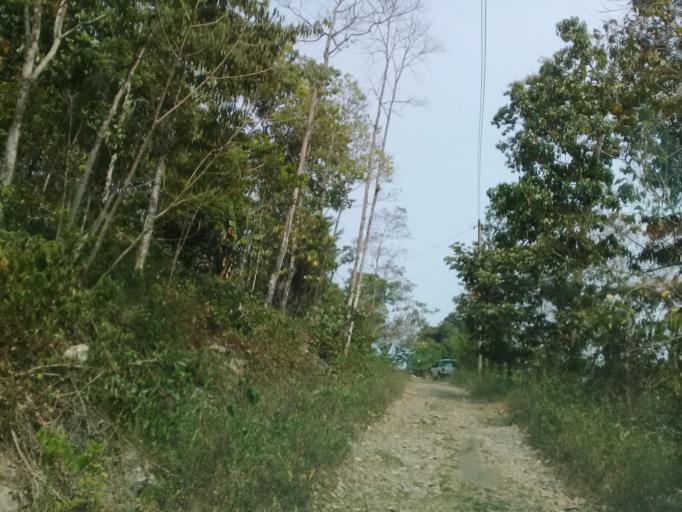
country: MX
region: Veracruz
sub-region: Tezonapa
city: Laguna Chica (Pueblo Nuevo)
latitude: 18.5825
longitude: -96.7549
